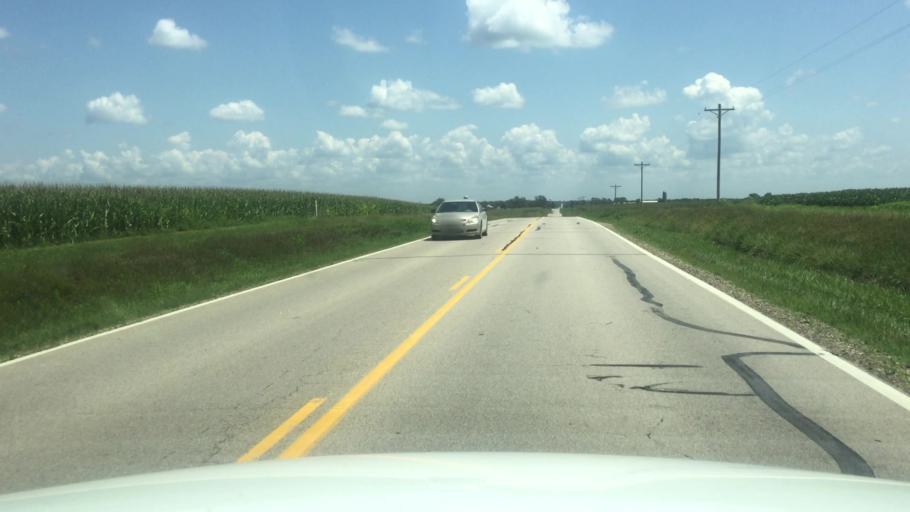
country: US
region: Kansas
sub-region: Brown County
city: Horton
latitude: 39.6674
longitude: -95.5984
